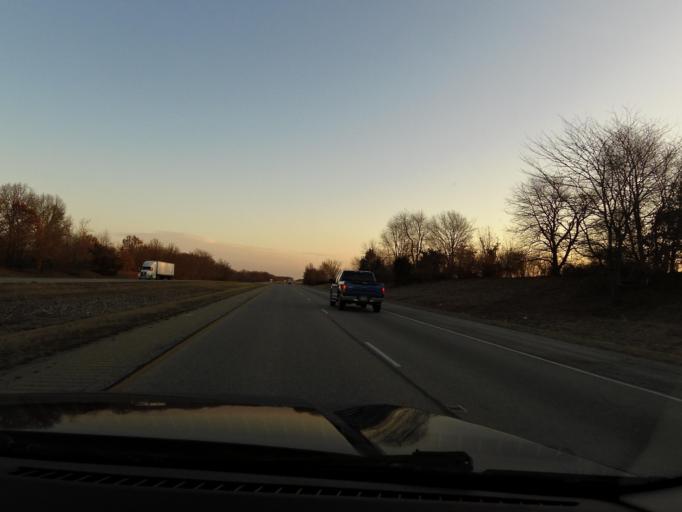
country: US
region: Illinois
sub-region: Marion County
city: Salem
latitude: 38.6943
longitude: -88.9634
